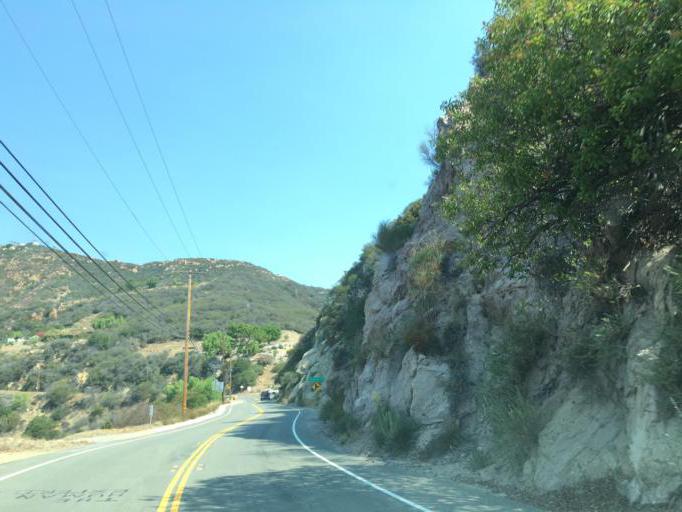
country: US
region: California
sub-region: Los Angeles County
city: Las Flores
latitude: 34.0685
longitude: -118.6530
